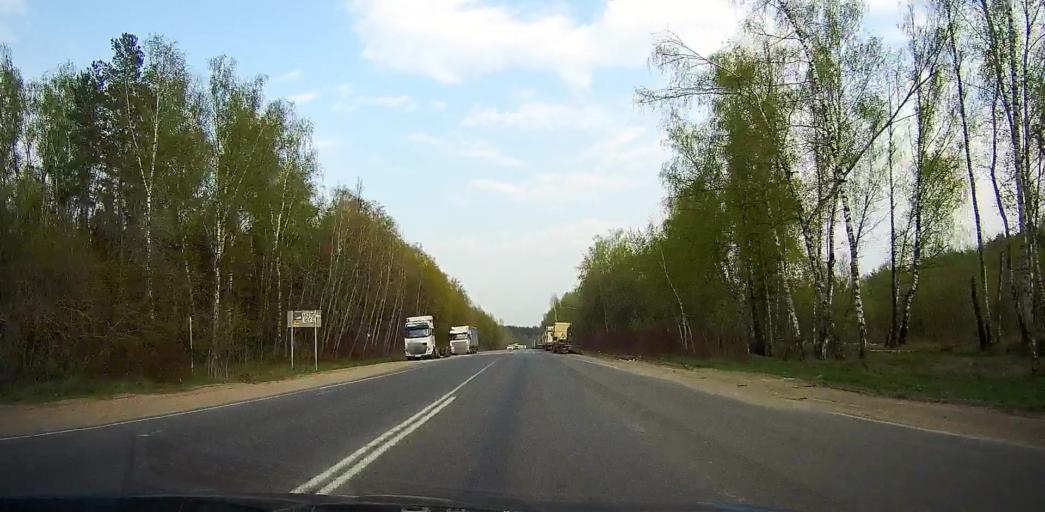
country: RU
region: Moskovskaya
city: Petrovskaya
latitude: 55.5318
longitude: 37.7713
